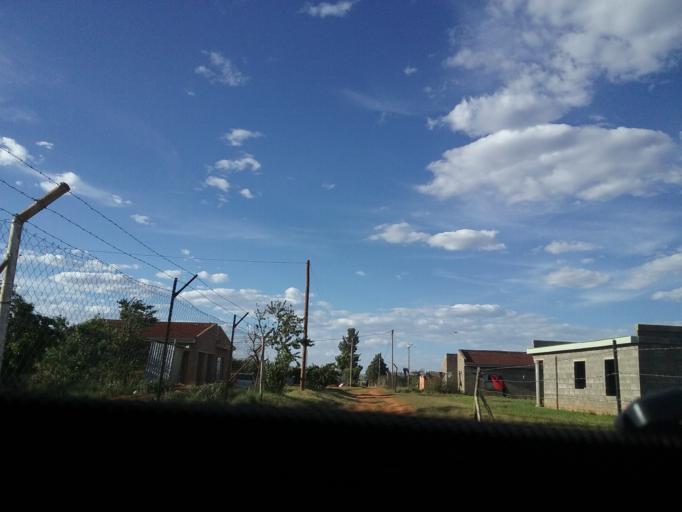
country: LS
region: Maseru
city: Maseru
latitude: -29.4313
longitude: 27.5711
